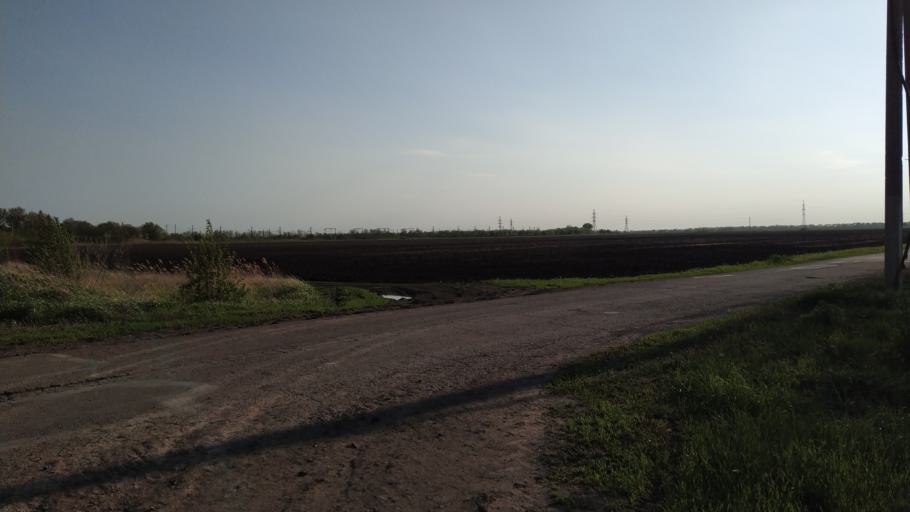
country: RU
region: Rostov
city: Bataysk
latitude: 47.0896
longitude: 39.7128
